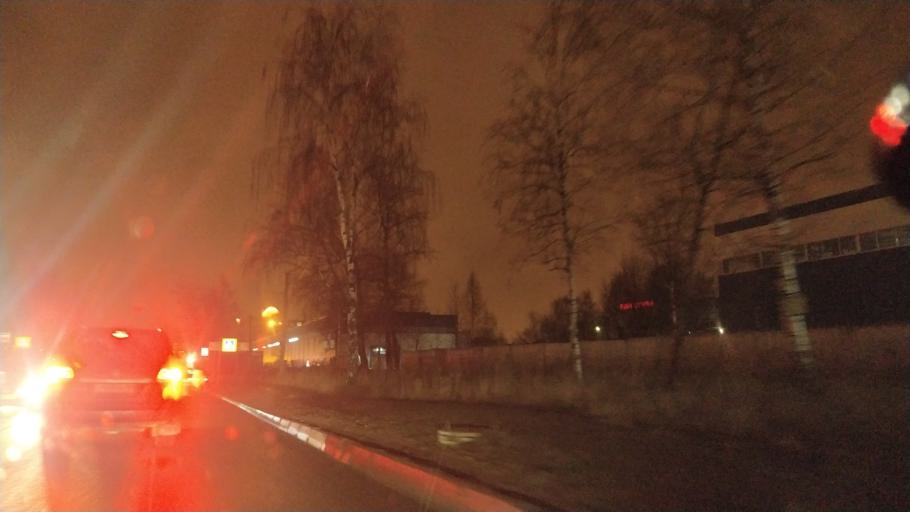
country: RU
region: Leningrad
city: Bugry
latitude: 60.0592
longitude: 30.3849
